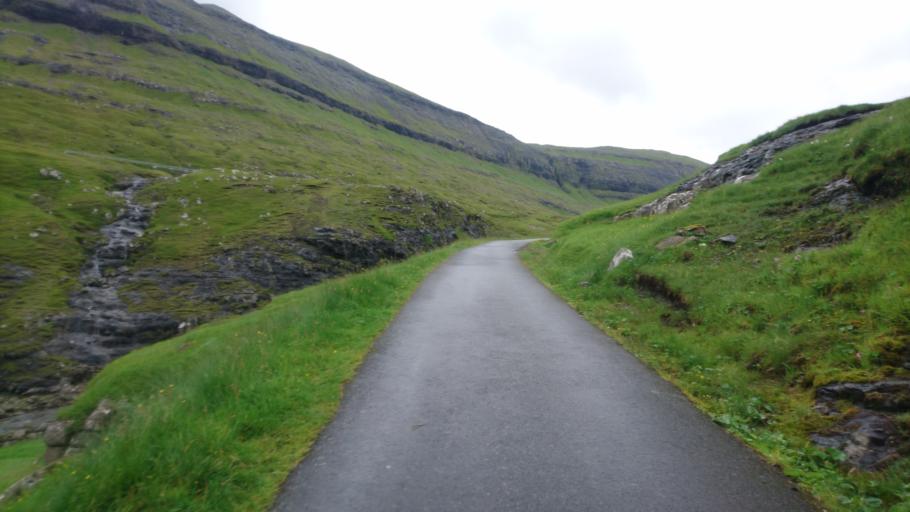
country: FO
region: Streymoy
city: Vestmanna
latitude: 62.2436
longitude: -7.1754
